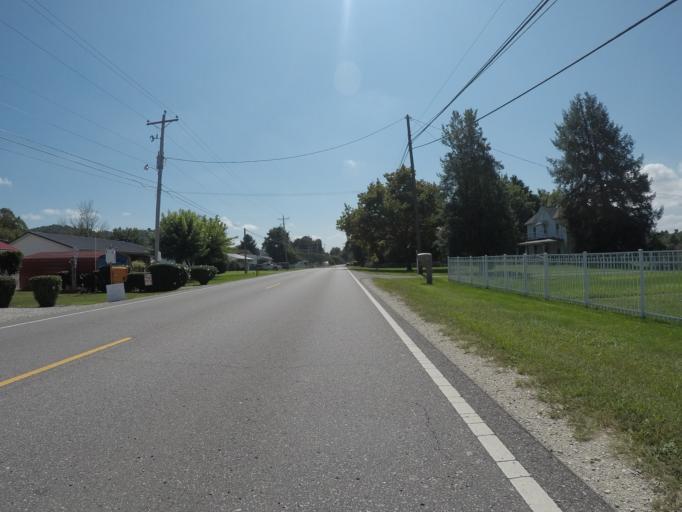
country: US
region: Kentucky
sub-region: Boyd County
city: Ashland
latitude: 38.4623
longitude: -82.5998
